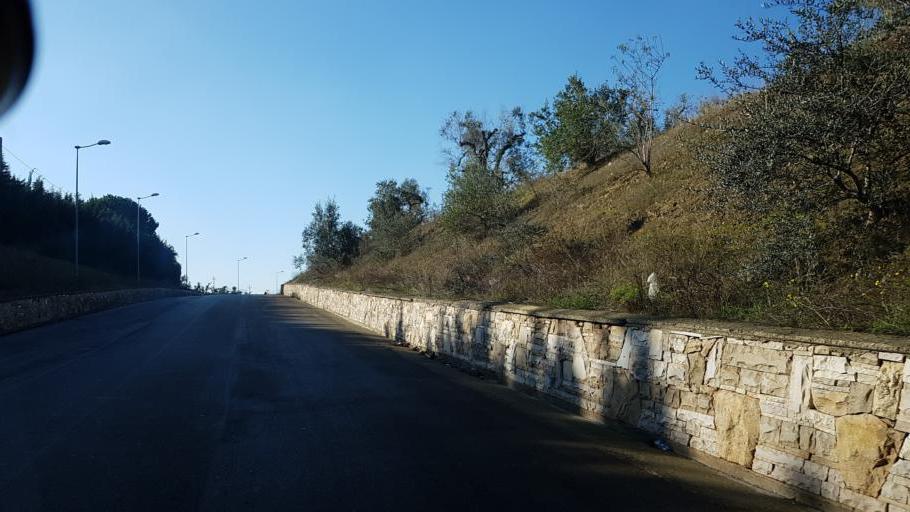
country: IT
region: Apulia
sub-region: Provincia di Lecce
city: Squinzano
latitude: 40.4296
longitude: 18.0557
